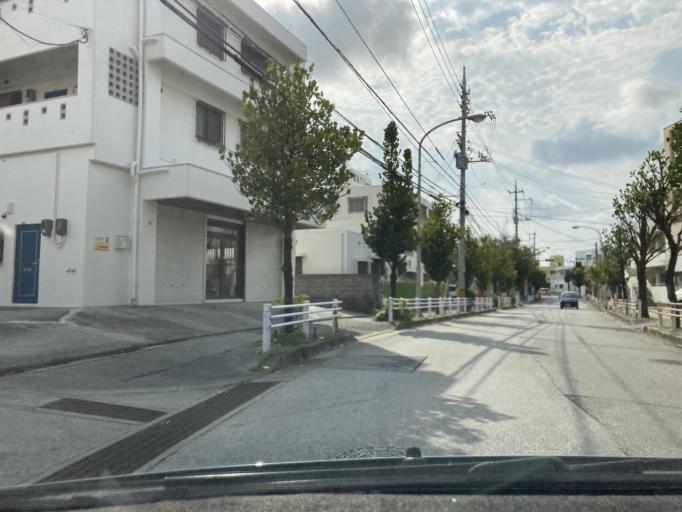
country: JP
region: Okinawa
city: Naha-shi
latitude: 26.2004
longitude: 127.7174
